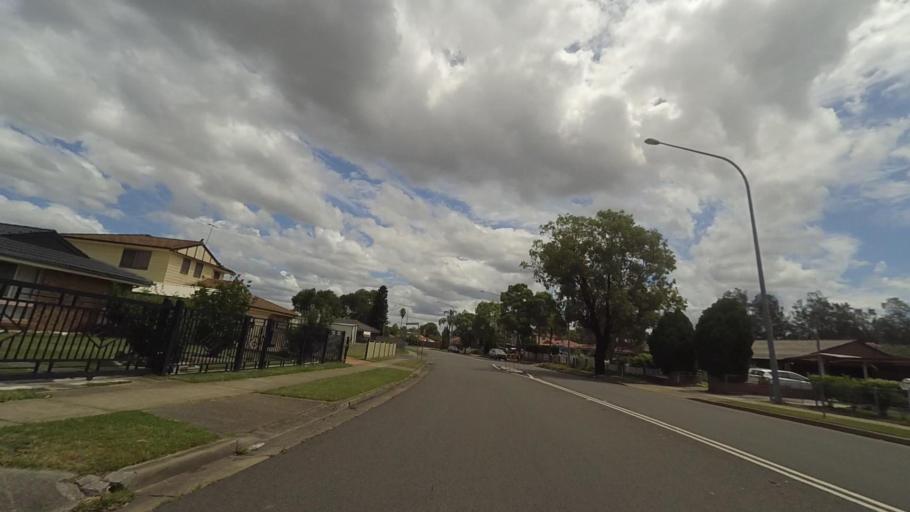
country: AU
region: New South Wales
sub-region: Fairfield
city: Fairfield Heights
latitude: -33.8677
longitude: 150.9122
